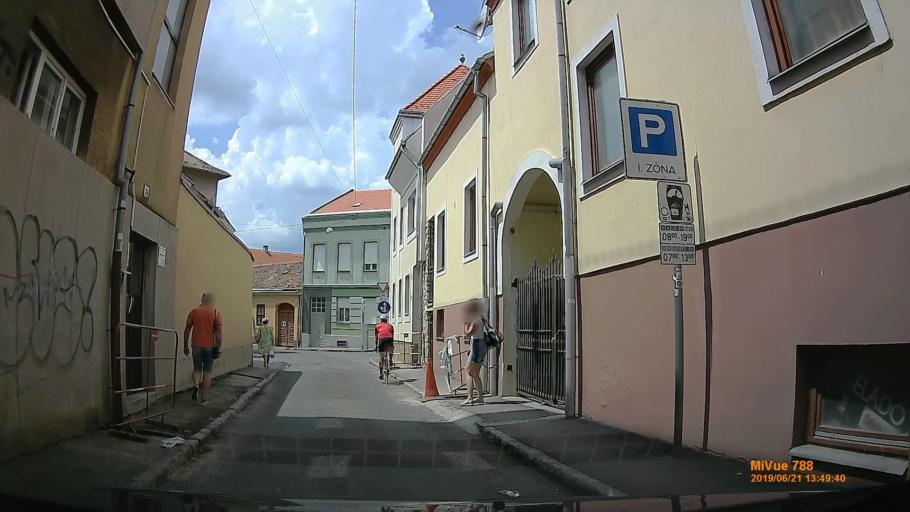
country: HU
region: Baranya
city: Pecs
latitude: 46.0755
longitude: 18.2348
